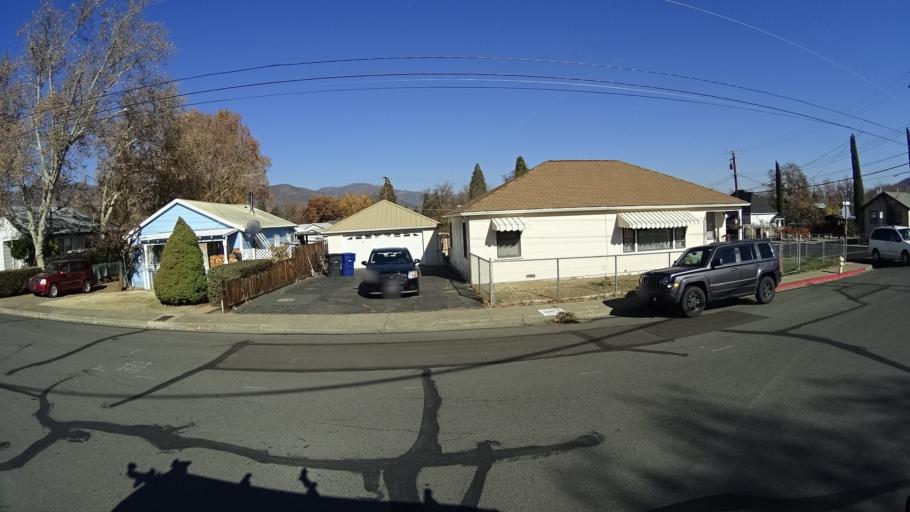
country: US
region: California
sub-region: Siskiyou County
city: Yreka
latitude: 41.7287
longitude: -122.6430
